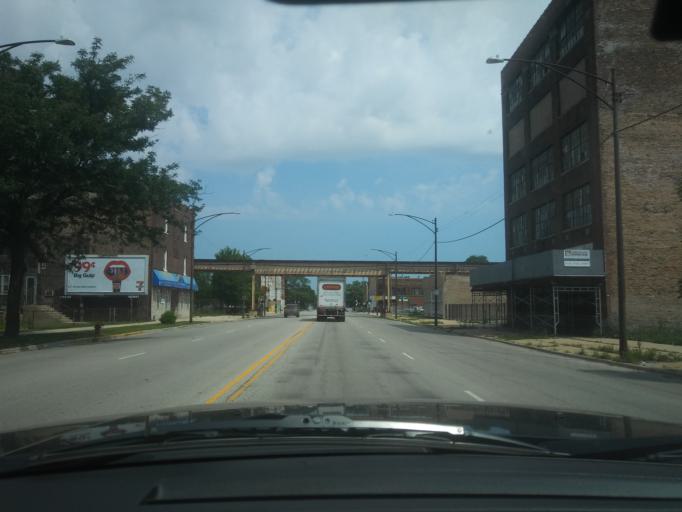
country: US
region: Illinois
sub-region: Cook County
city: Chicago
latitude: 41.7861
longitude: -87.6255
